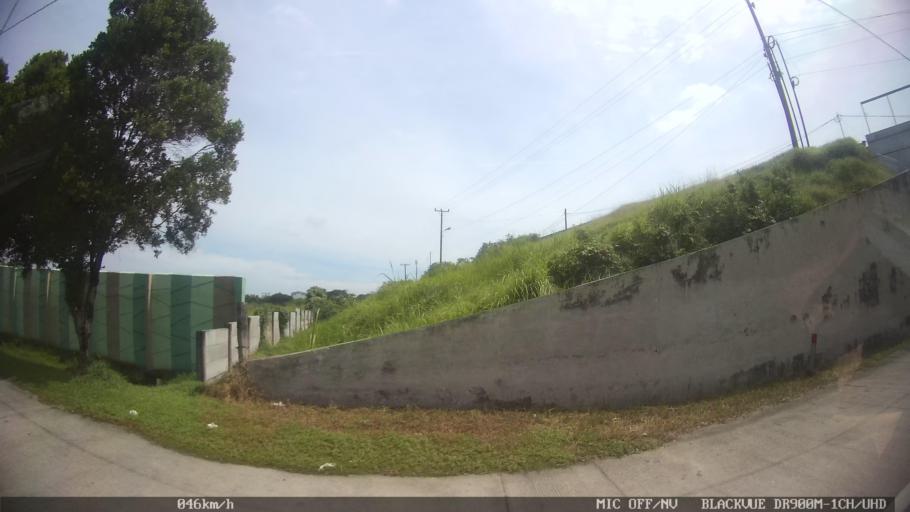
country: ID
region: North Sumatra
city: Medan
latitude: 3.6368
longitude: 98.7072
